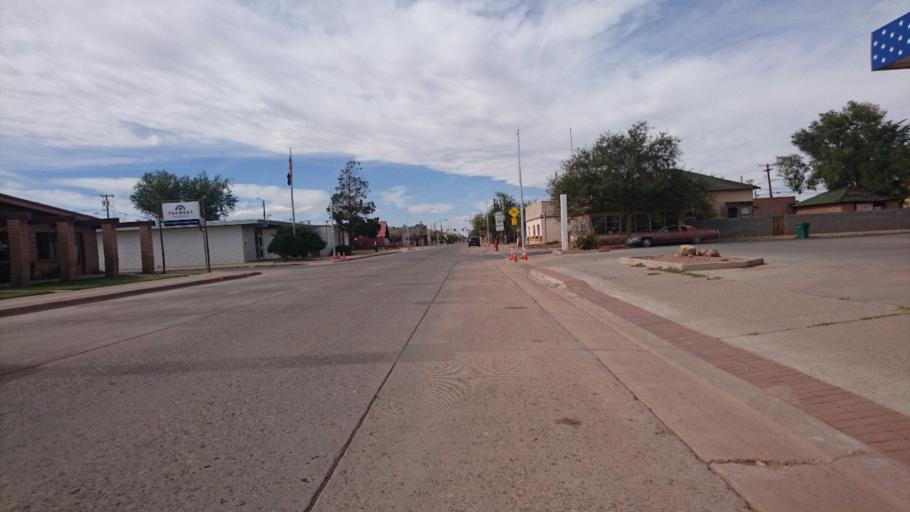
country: US
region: Arizona
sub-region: Navajo County
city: Winslow
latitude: 35.0229
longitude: -110.6939
